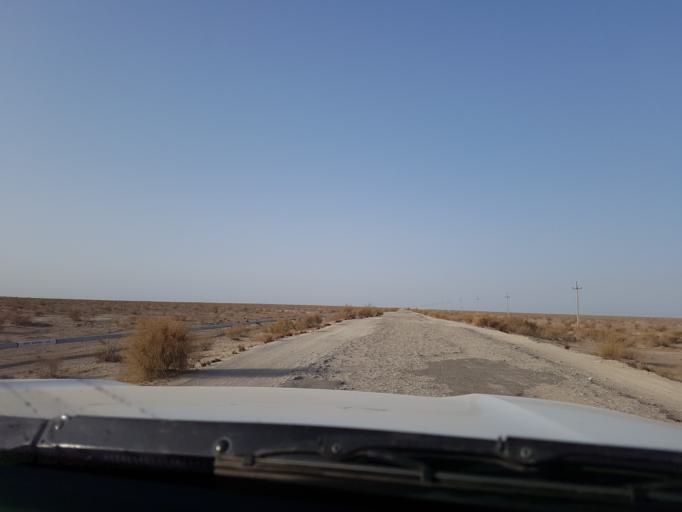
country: UZ
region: Karakalpakstan
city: Shumanay Shahri
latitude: 42.0088
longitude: 58.0893
